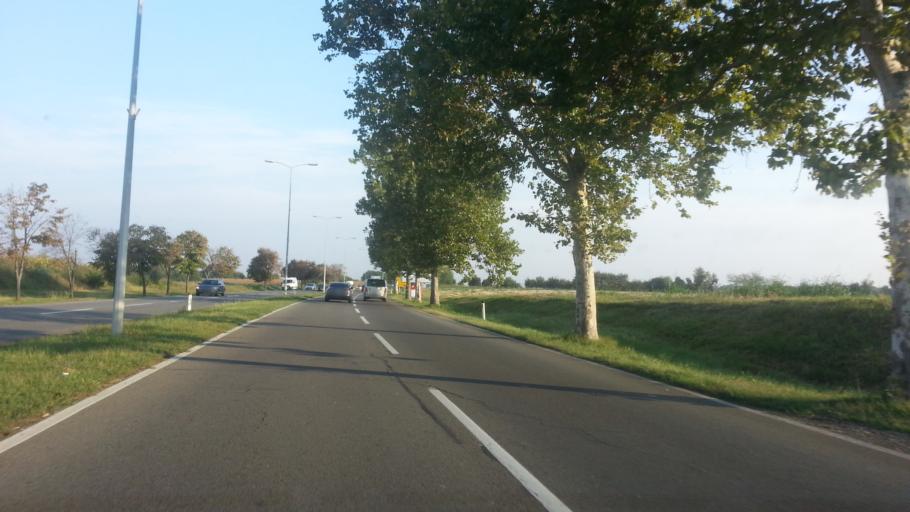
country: RS
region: Central Serbia
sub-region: Belgrade
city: Surcin
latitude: 44.8261
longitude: 20.2804
